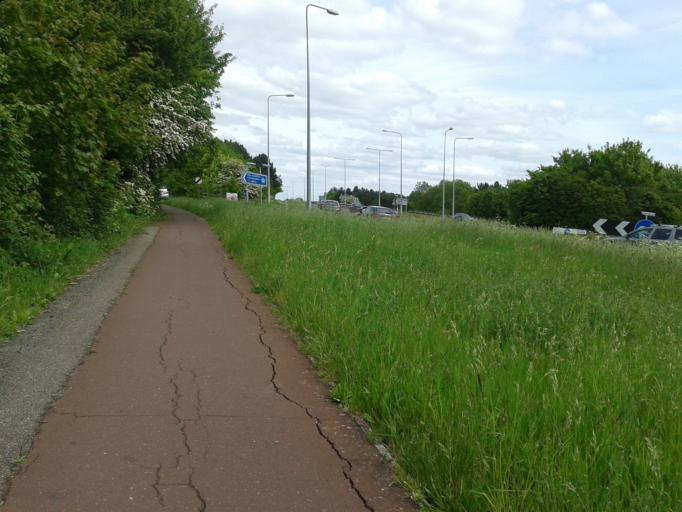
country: GB
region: England
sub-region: Cambridgeshire
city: Barton
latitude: 52.1870
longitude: 0.0720
